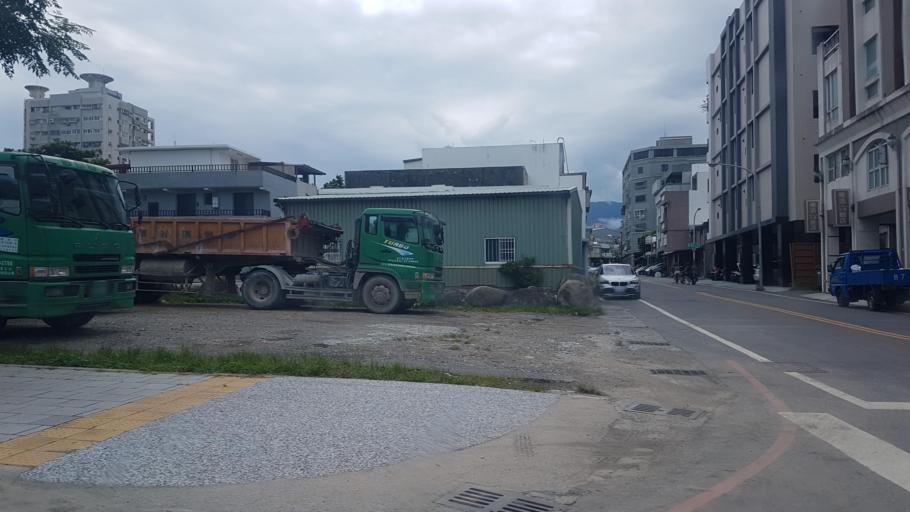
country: TW
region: Taiwan
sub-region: Hualien
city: Hualian
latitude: 23.9940
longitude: 121.6335
